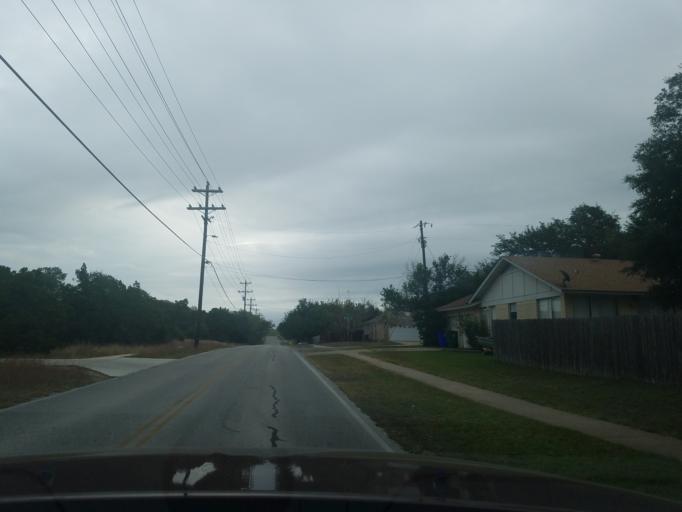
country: US
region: Texas
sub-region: Williamson County
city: Cedar Park
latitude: 30.4811
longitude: -97.8110
